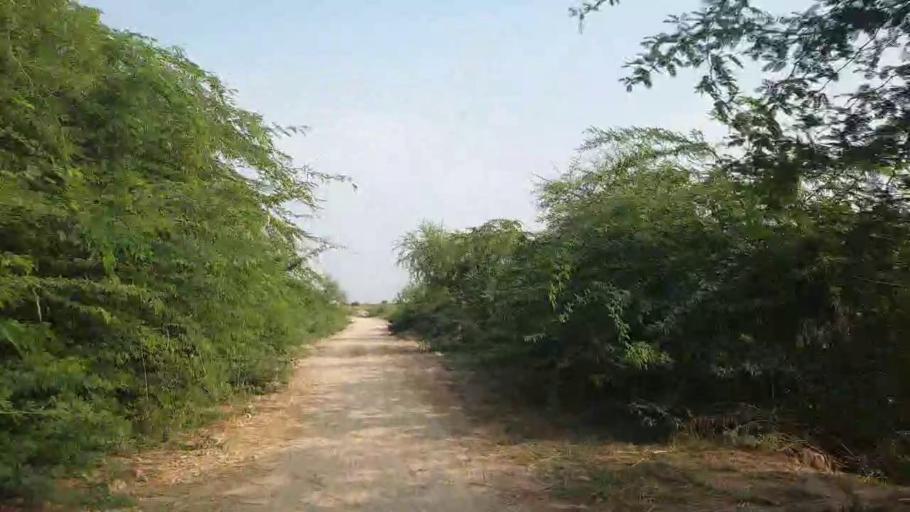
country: PK
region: Sindh
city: Kadhan
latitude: 24.4594
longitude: 68.7960
